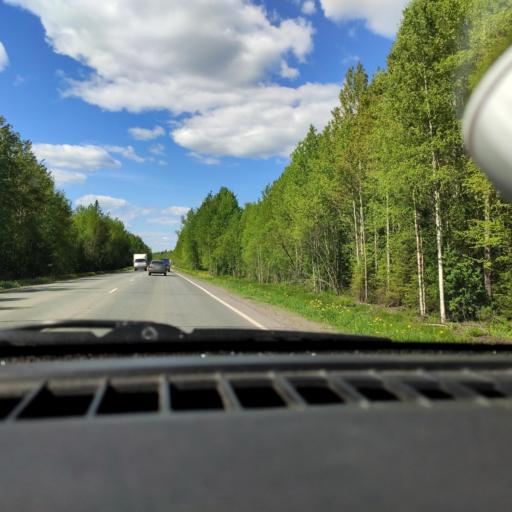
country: RU
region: Perm
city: Polazna
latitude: 58.2862
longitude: 56.1639
